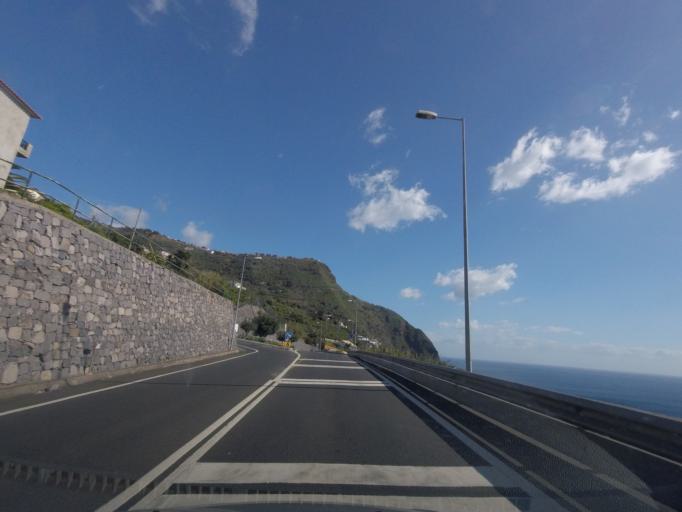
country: PT
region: Madeira
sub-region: Calheta
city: Arco da Calheta
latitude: 32.7117
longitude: -17.1532
